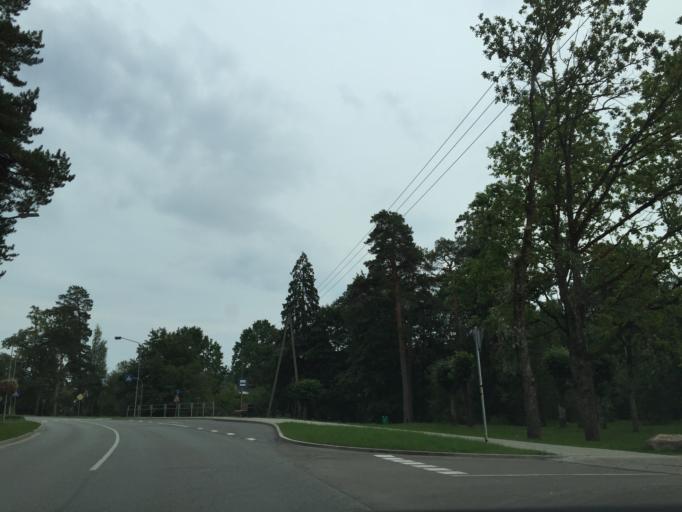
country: LV
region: Ogre
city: Ogre
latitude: 56.8169
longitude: 24.6187
